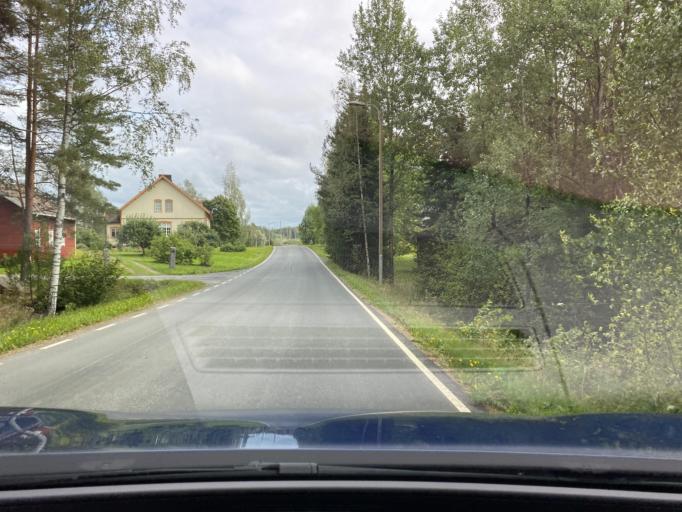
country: FI
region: Pirkanmaa
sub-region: Lounais-Pirkanmaa
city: Punkalaidun
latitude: 61.2317
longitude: 23.1317
